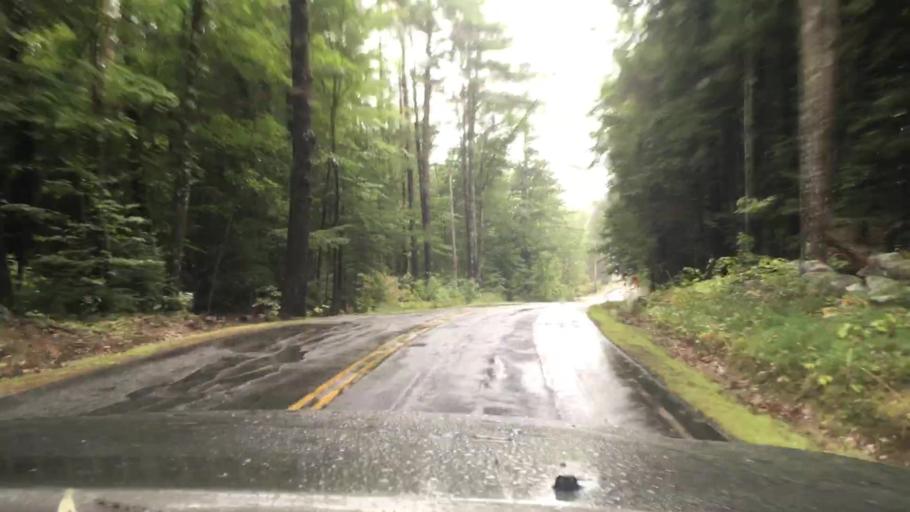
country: US
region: New Hampshire
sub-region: Belknap County
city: Meredith
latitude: 43.6705
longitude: -71.5333
